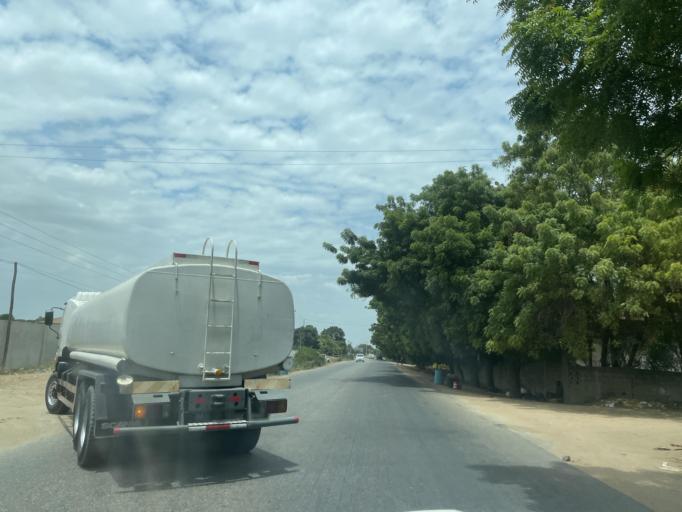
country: AO
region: Luanda
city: Luanda
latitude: -8.9250
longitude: 13.3979
